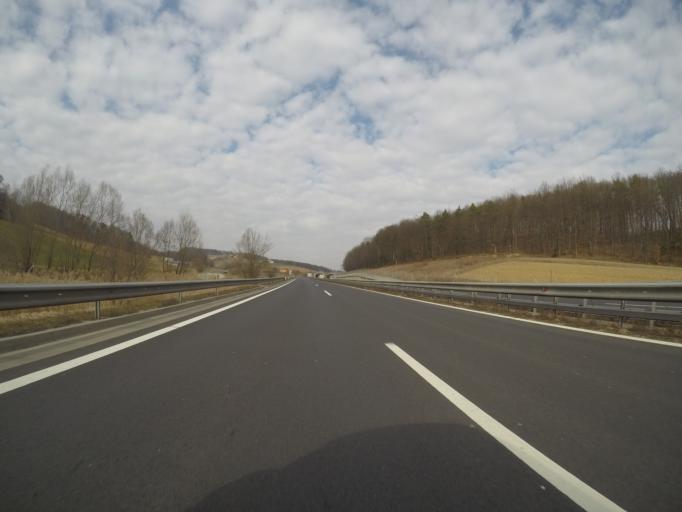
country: SI
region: Cerkvenjak
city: Cerkvenjak
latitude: 46.5675
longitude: 15.9288
